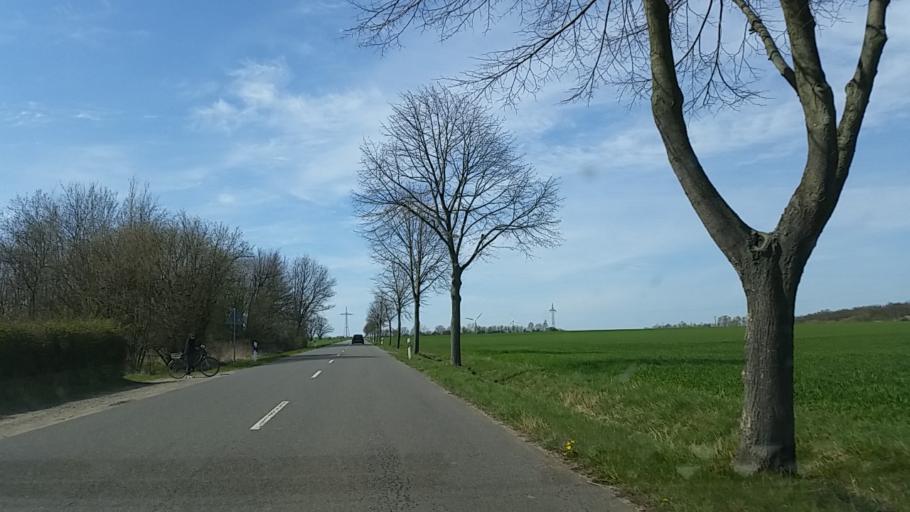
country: DE
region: Lower Saxony
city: Gross Twulpstedt
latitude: 52.3549
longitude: 10.9035
